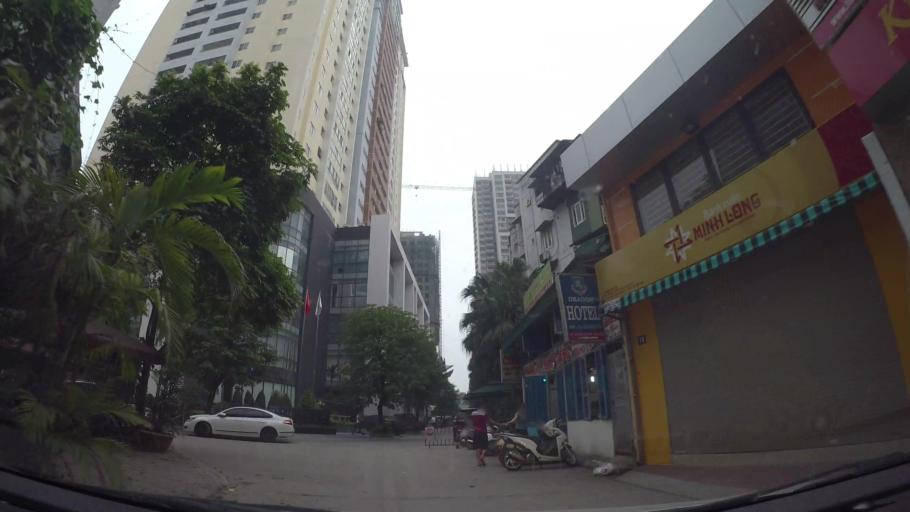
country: VN
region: Ha Noi
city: Cau Dien
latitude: 21.0355
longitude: 105.7718
